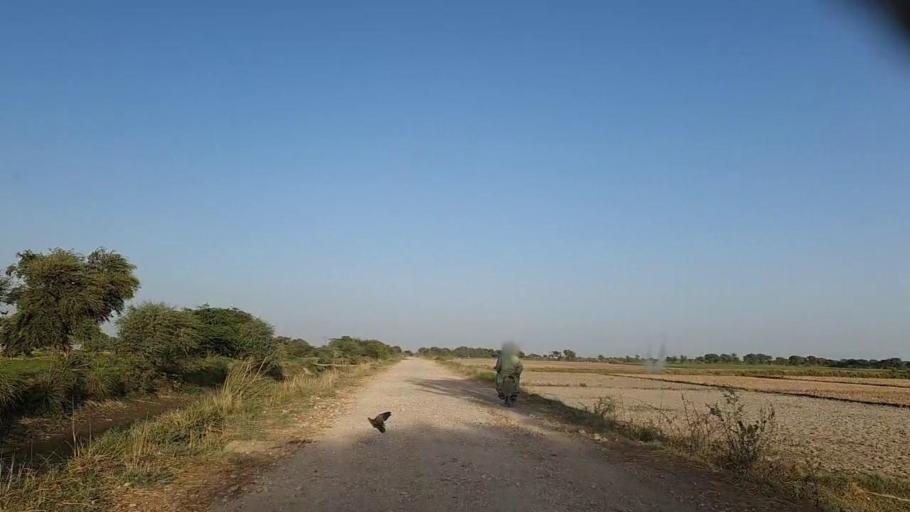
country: PK
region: Sindh
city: Jati
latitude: 24.4142
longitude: 68.3186
